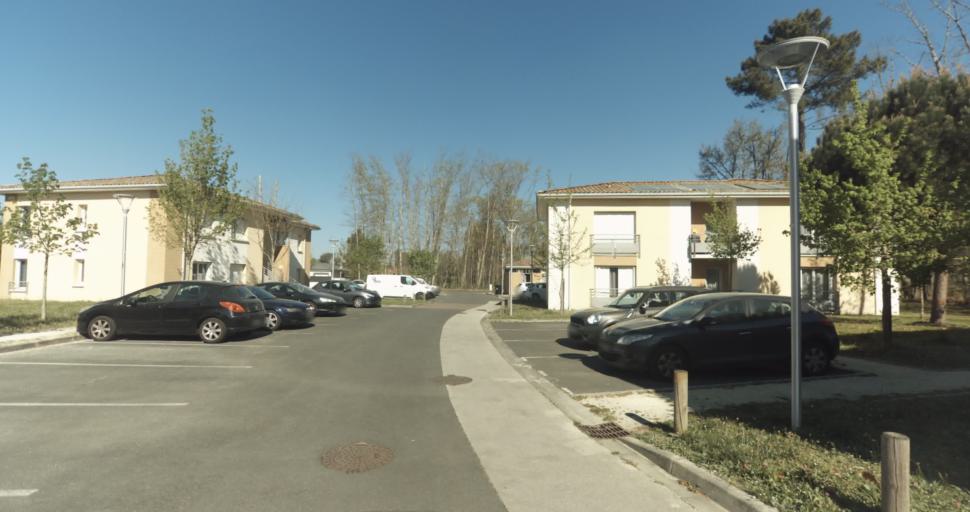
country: FR
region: Aquitaine
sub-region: Departement de la Gironde
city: Martignas-sur-Jalle
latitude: 44.7966
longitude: -0.8347
